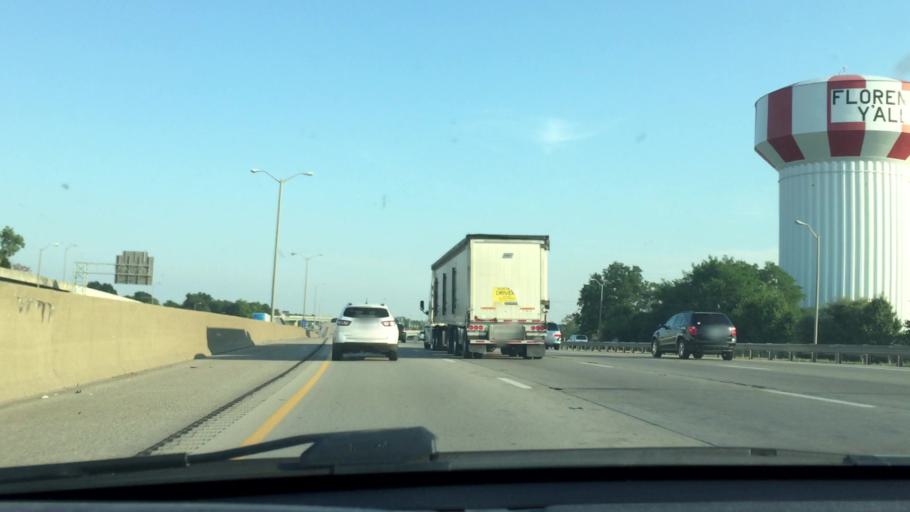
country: US
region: Kentucky
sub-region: Boone County
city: Florence
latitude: 38.9988
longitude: -84.6474
